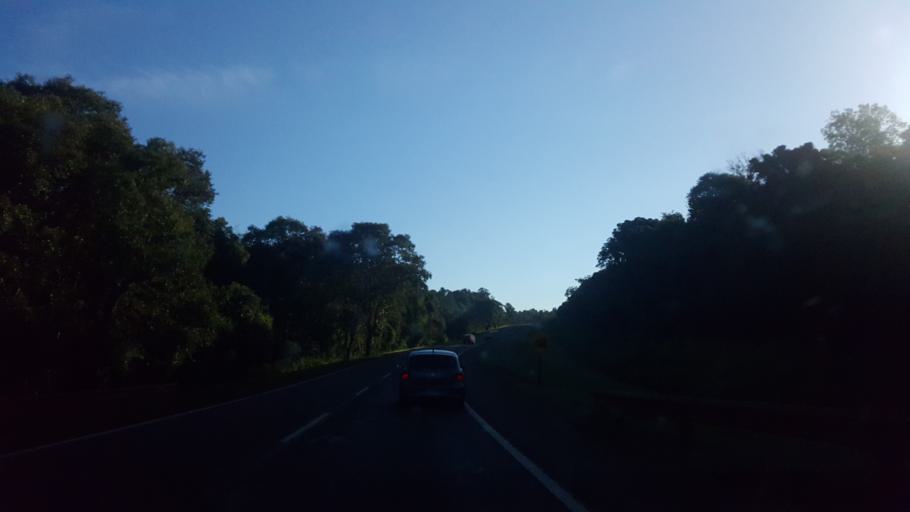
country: AR
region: Misiones
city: El Alcazar
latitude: -26.7188
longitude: -54.8565
